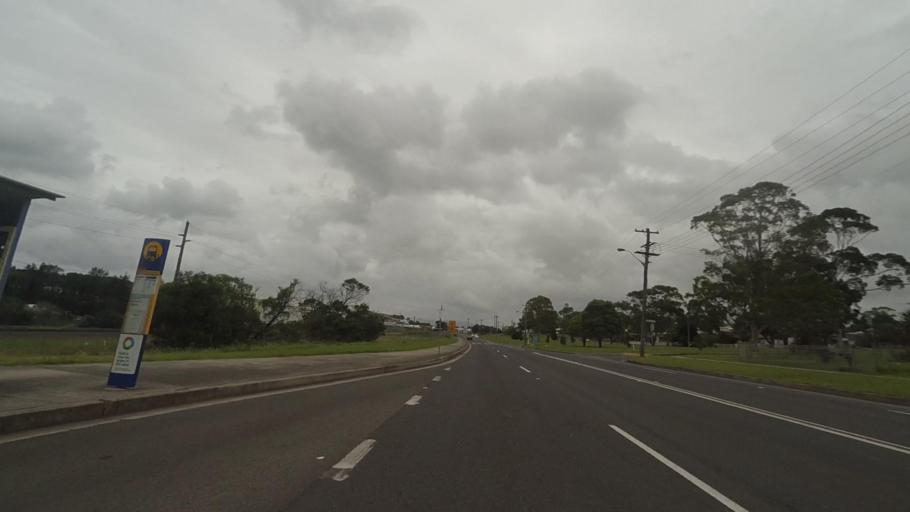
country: AU
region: New South Wales
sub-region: Wollongong
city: Cordeaux Heights
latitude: -34.4628
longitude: 150.8377
